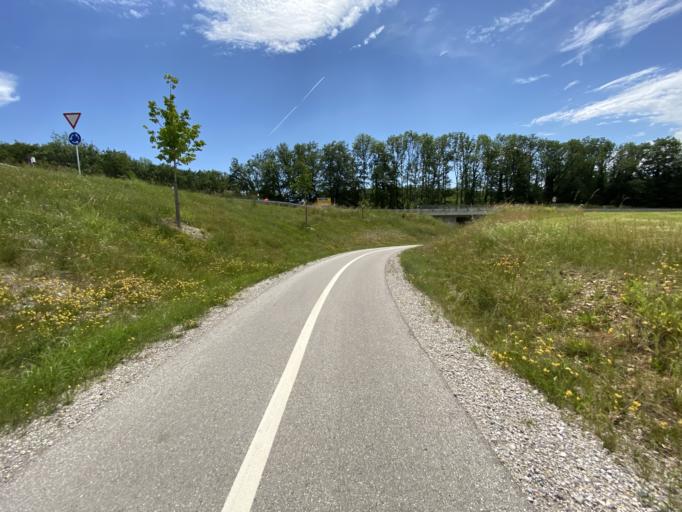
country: DE
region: Bavaria
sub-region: Upper Bavaria
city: Wessling
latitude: 48.0669
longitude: 11.2406
